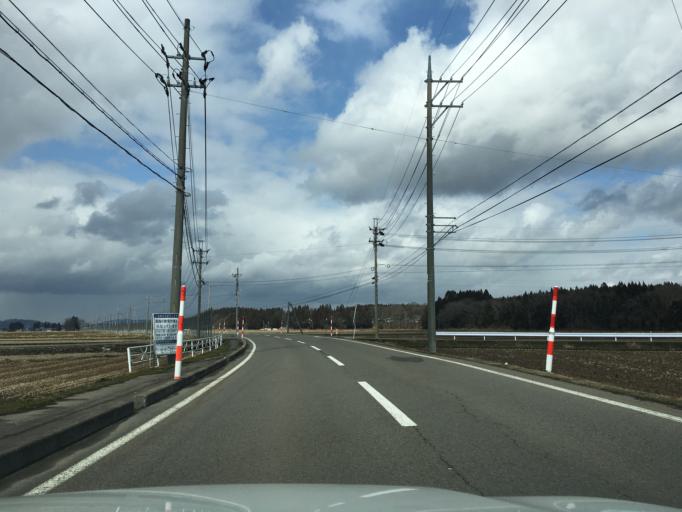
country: JP
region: Akita
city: Takanosu
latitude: 40.1262
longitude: 140.3651
